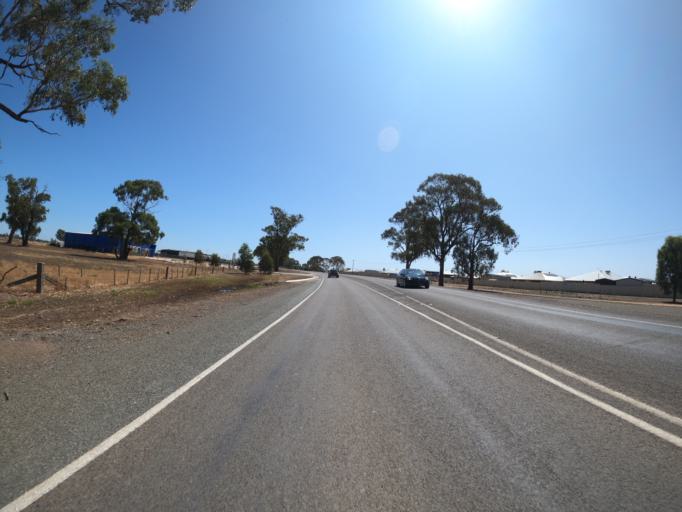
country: AU
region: Victoria
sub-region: Moira
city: Yarrawonga
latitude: -36.0103
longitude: 146.0297
